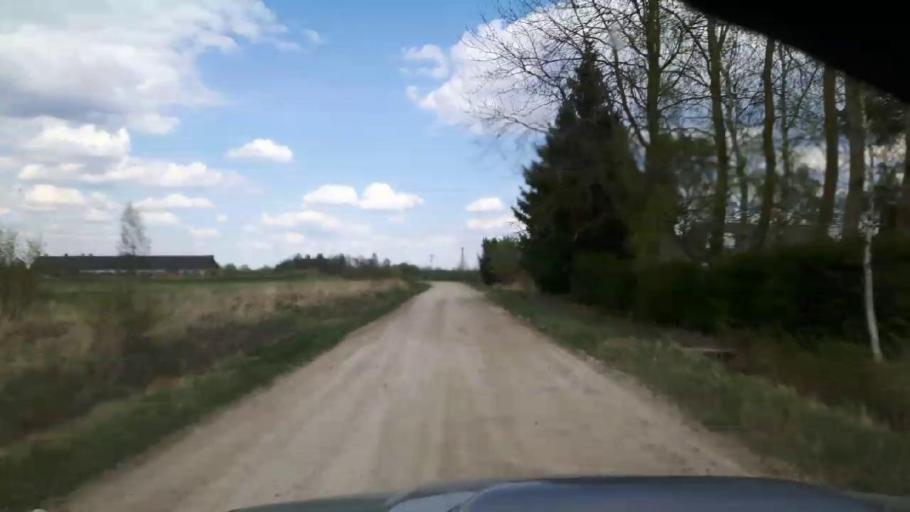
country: EE
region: Paernumaa
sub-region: Sindi linn
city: Sindi
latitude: 58.4100
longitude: 24.6954
